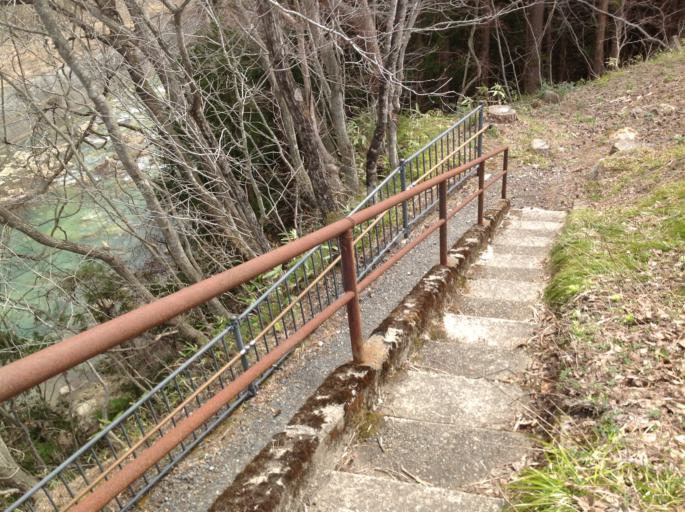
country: JP
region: Iwate
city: Ichinoseki
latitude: 38.9862
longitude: 140.9120
